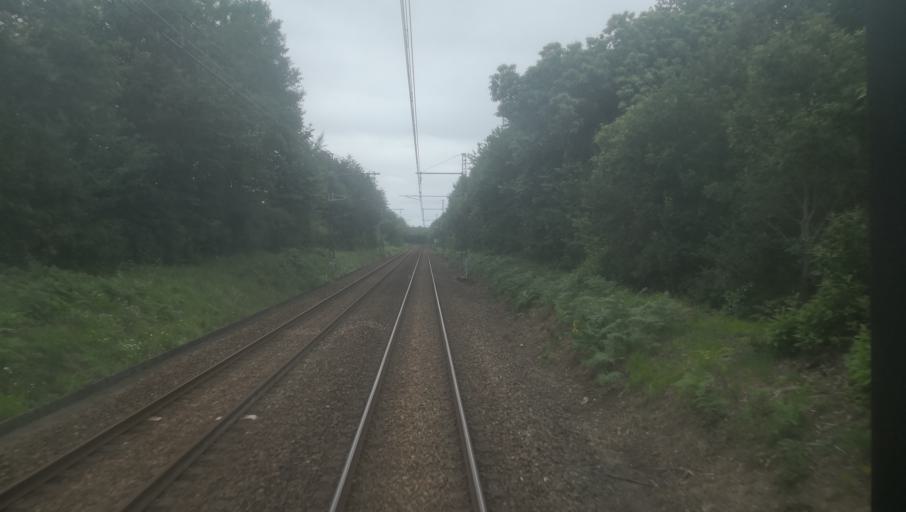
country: FR
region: Centre
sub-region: Departement de l'Indre
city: Chantome
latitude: 46.4499
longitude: 1.5512
